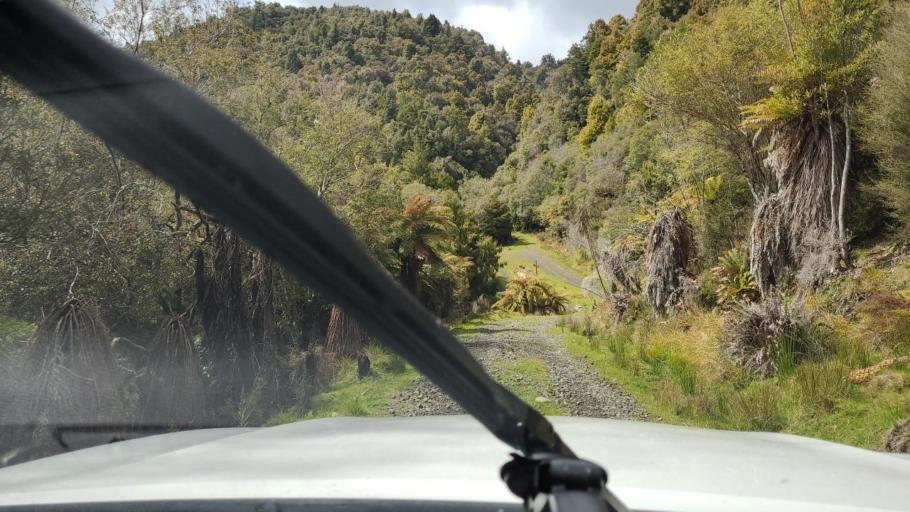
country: NZ
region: Bay of Plenty
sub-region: Opotiki District
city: Opotiki
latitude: -38.2042
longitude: 177.6116
